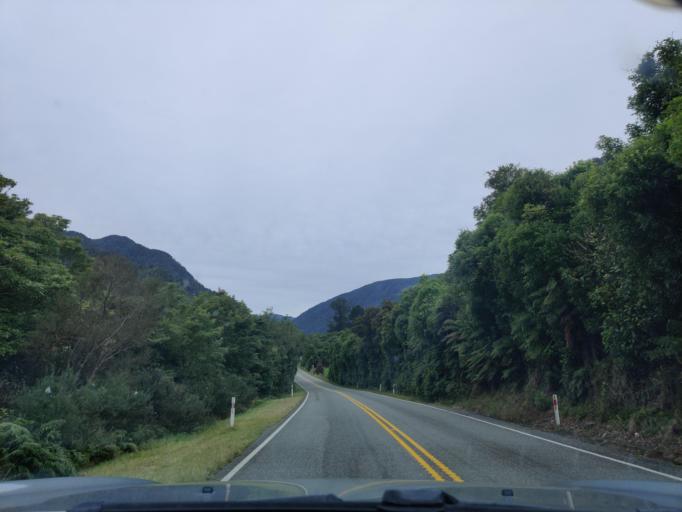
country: NZ
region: West Coast
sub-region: Buller District
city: Westport
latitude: -41.8312
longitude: 171.6513
